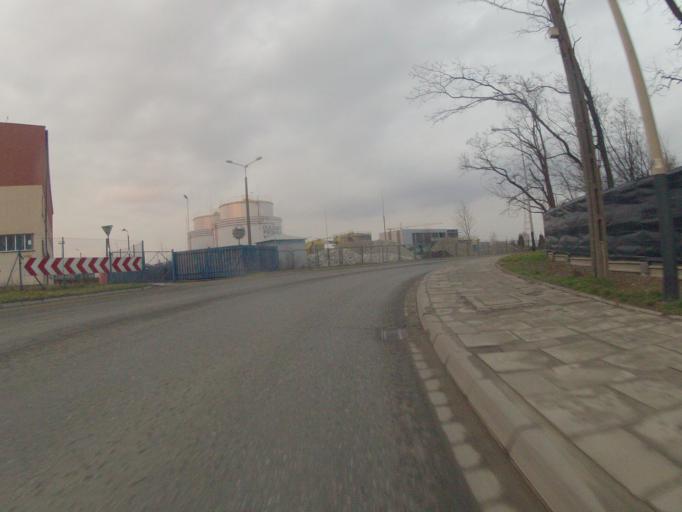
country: PL
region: Lesser Poland Voivodeship
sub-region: Powiat wielicki
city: Czarnochowice
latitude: 50.0516
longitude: 20.0149
